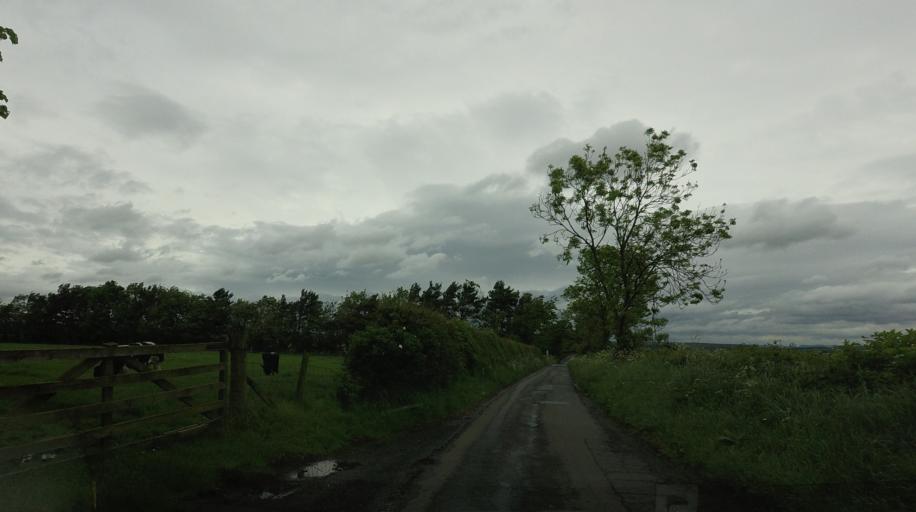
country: GB
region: Scotland
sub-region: West Lothian
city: Broxburn
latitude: 55.9221
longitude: -3.4444
